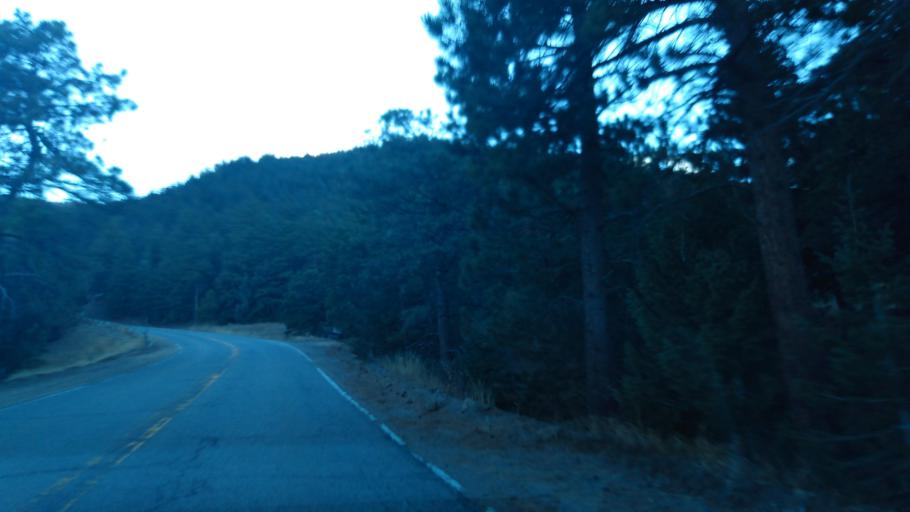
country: US
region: Colorado
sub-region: Boulder County
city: Coal Creek
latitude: 39.9867
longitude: -105.3736
